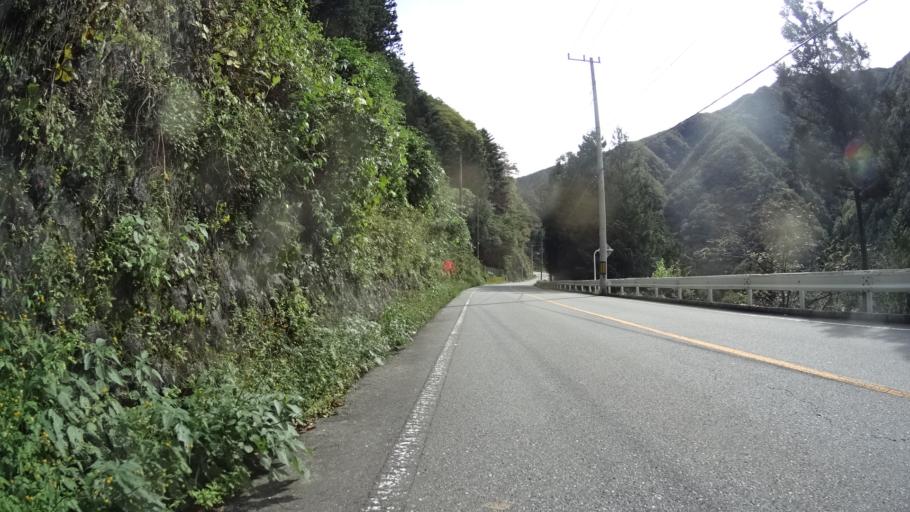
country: JP
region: Yamanashi
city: Otsuki
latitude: 35.7877
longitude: 138.9453
